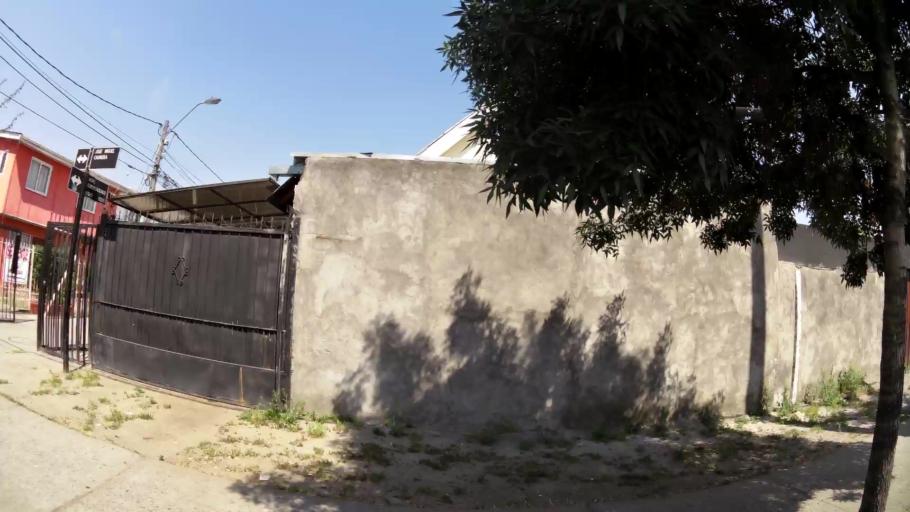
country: CL
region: Santiago Metropolitan
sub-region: Provincia de Santiago
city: La Pintana
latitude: -33.5507
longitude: -70.6075
